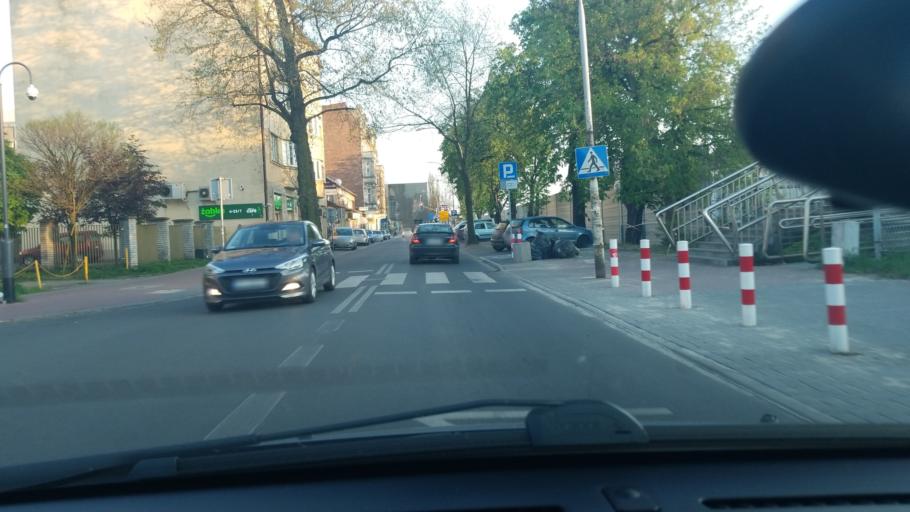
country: PL
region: Silesian Voivodeship
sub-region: Czestochowa
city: Czestochowa
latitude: 50.8134
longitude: 19.1218
